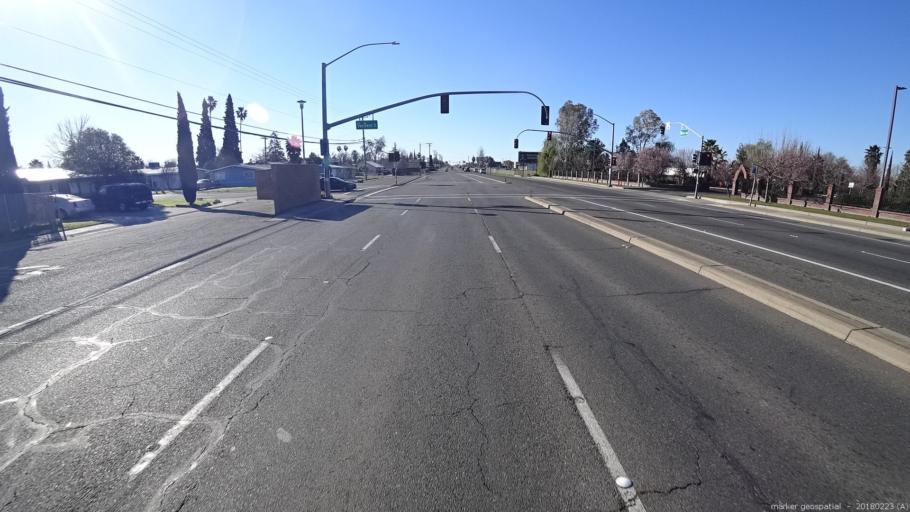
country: US
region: California
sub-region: Sacramento County
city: North Highlands
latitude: 38.6867
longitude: -121.3829
